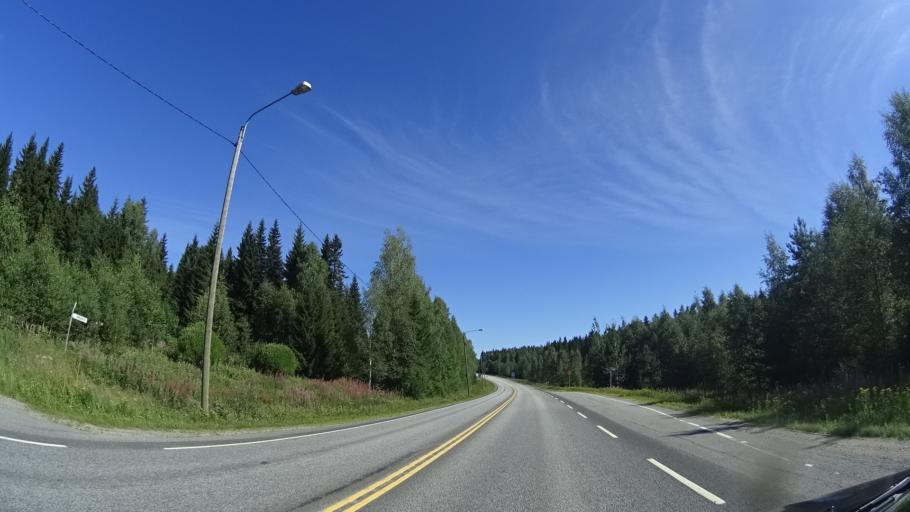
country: FI
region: Central Finland
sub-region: AEaenekoski
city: AEaenekoski
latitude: 62.8280
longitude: 25.8133
